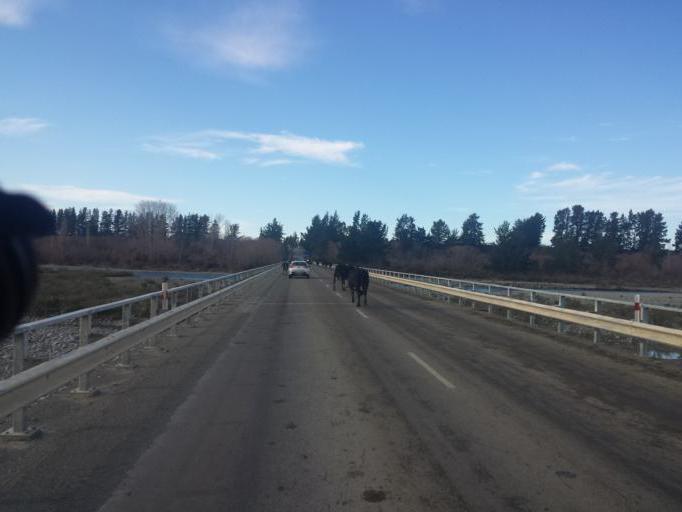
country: NZ
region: Canterbury
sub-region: Timaru District
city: Pleasant Point
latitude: -43.9742
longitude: 171.3008
